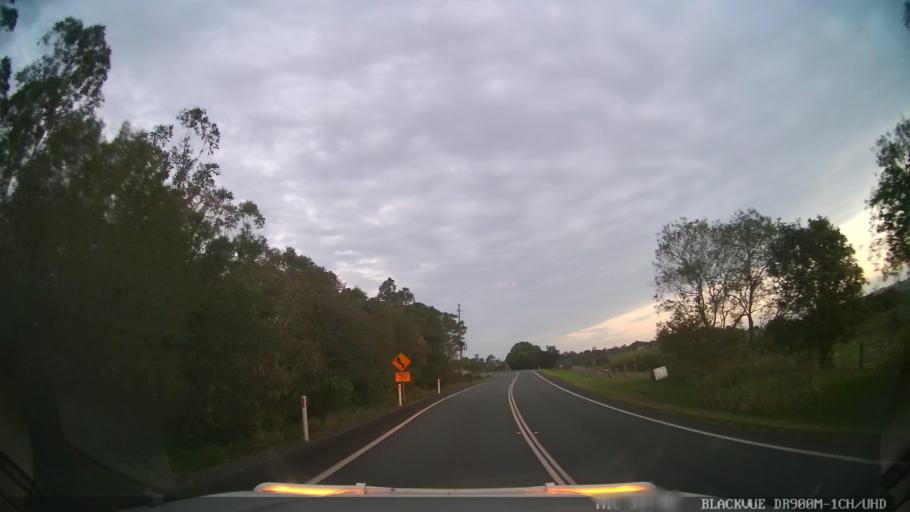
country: AU
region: Queensland
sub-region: Sunshine Coast
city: Nambour
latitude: -26.6191
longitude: 152.9042
